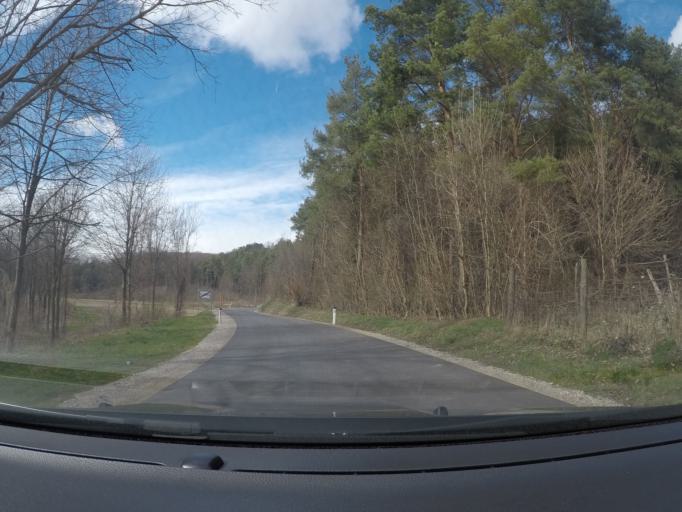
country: AT
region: Lower Austria
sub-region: Politischer Bezirk Neunkirchen
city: Pitten
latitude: 47.7279
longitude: 16.1967
